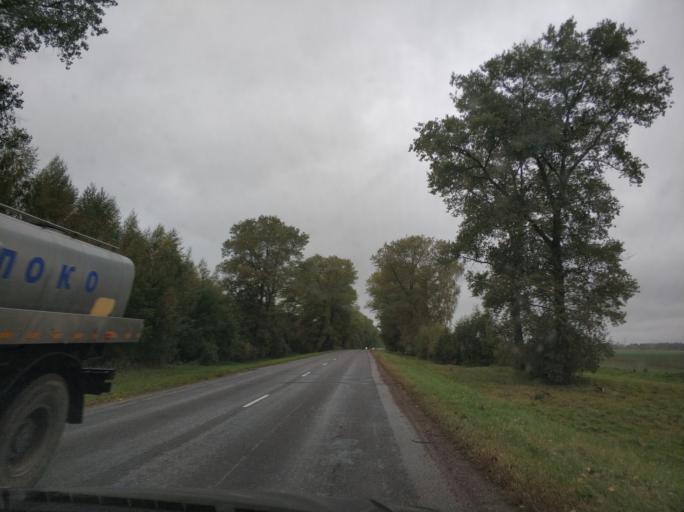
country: BY
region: Vitebsk
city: Polatsk
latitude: 55.4329
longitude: 28.9866
